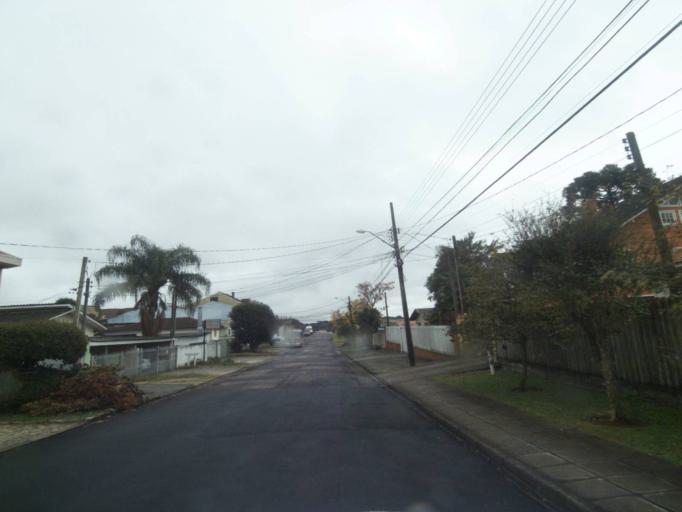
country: BR
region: Parana
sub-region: Curitiba
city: Curitiba
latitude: -25.5103
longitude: -49.3013
